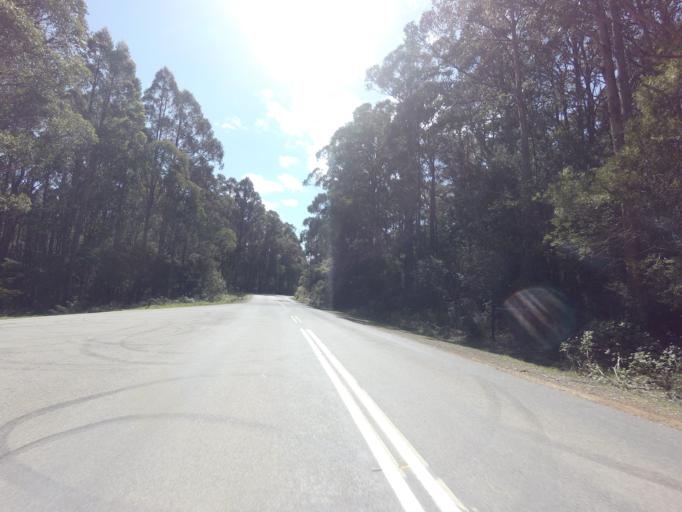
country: AU
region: Tasmania
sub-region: Derwent Valley
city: New Norfolk
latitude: -42.7276
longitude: 146.6738
